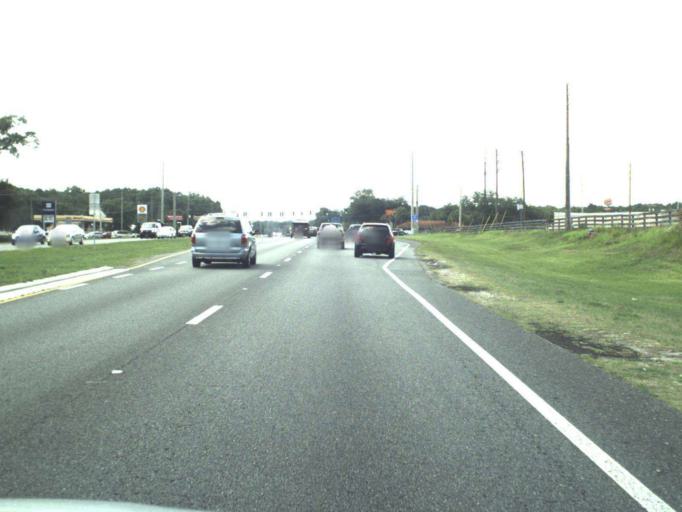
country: US
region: Florida
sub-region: Marion County
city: Ocala
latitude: 29.1566
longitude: -82.0850
